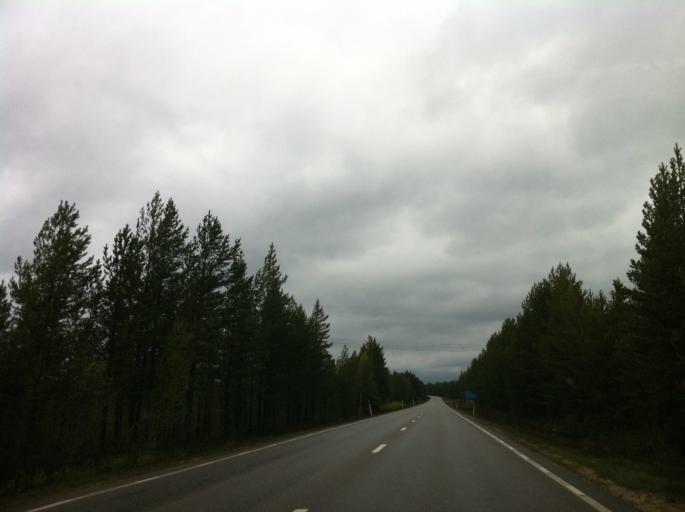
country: SE
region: Jaemtland
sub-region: Harjedalens Kommun
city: Sveg
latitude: 62.0538
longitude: 14.3059
